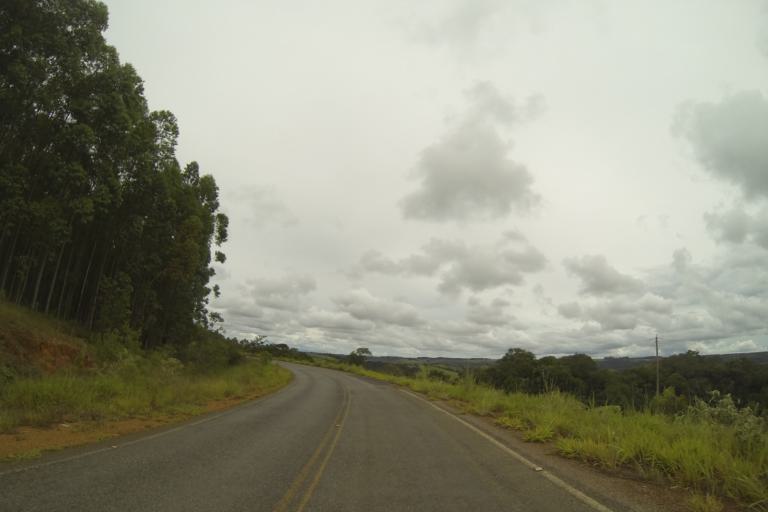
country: BR
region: Minas Gerais
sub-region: Ibia
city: Ibia
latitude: -19.6948
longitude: -46.4424
